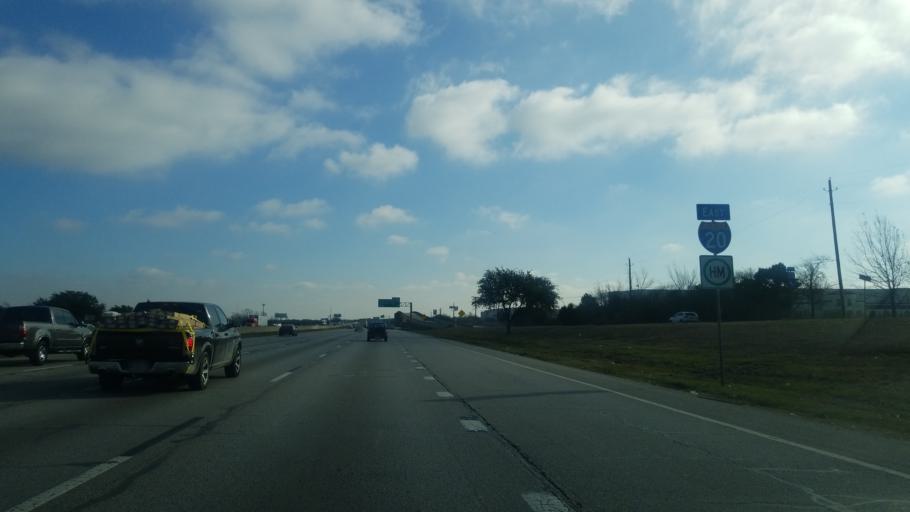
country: US
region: Texas
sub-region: Dallas County
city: DeSoto
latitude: 32.6422
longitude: -96.8150
